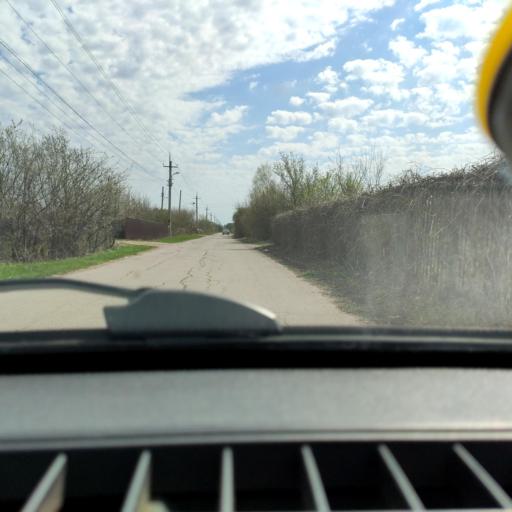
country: RU
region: Samara
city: Tol'yatti
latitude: 53.7003
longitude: 49.4369
